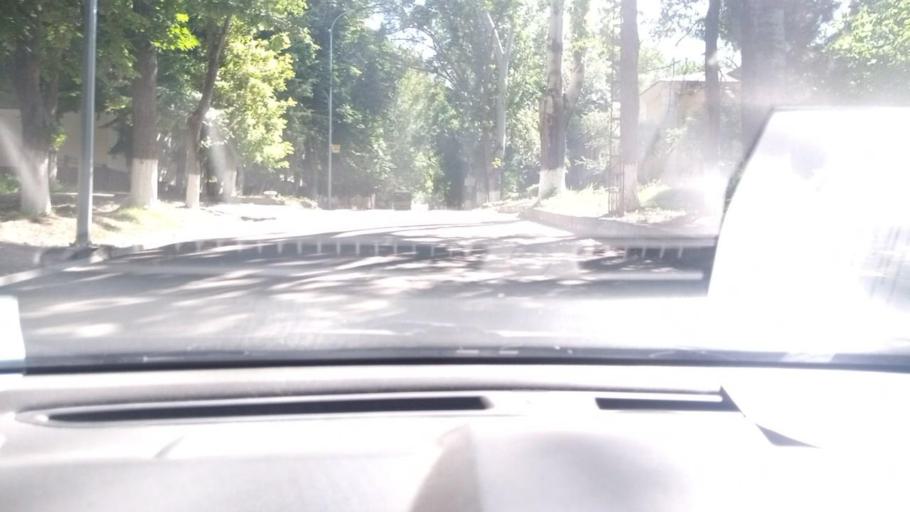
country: UZ
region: Toshkent
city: Yangiobod
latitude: 41.1195
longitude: 70.0944
